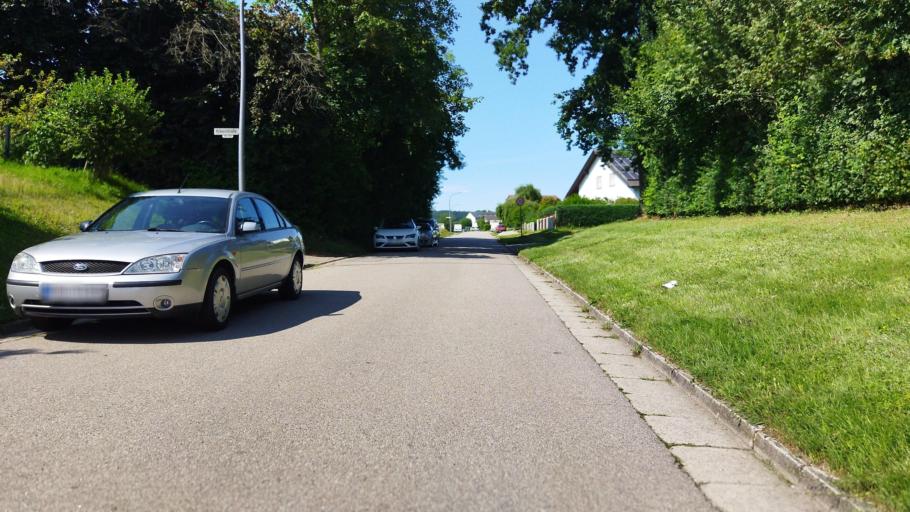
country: DE
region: Bavaria
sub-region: Lower Bavaria
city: Bad Abbach
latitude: 48.9313
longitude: 12.0155
